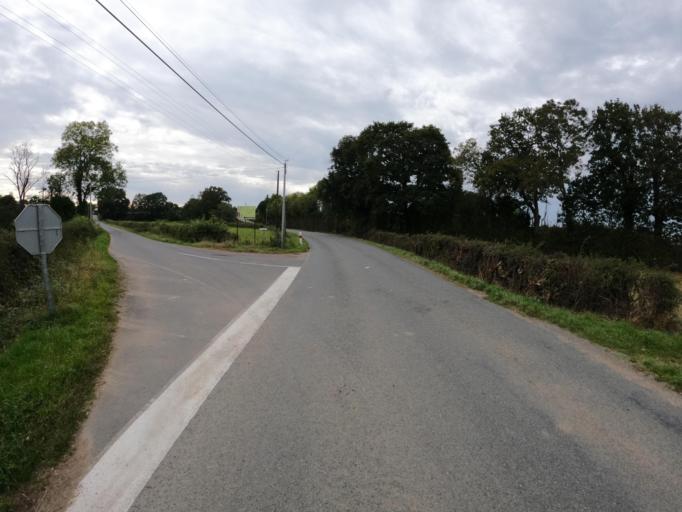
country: FR
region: Pays de la Loire
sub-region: Departement de Maine-et-Loire
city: Saint-Christophe-du-Bois
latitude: 47.0248
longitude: -0.9710
